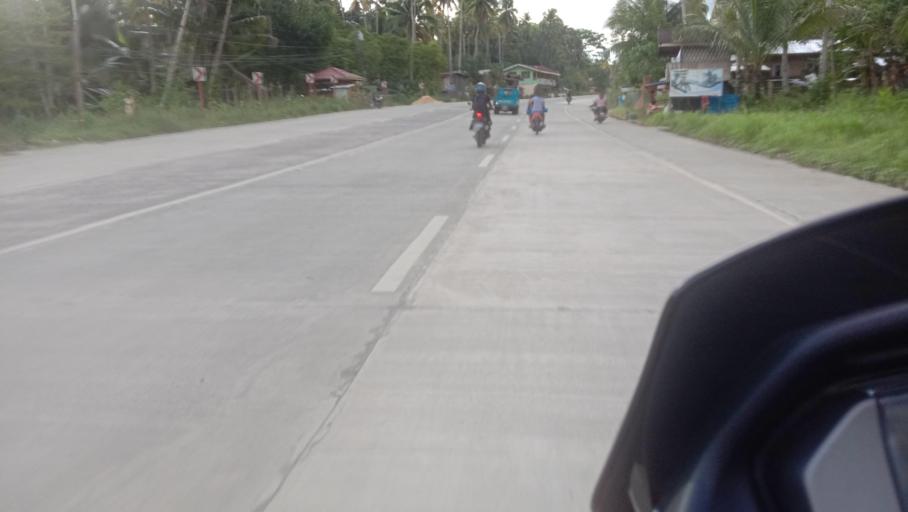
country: PH
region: Caraga
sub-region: Province of Surigao del Sur
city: Barobo
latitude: 8.5184
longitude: 126.1225
